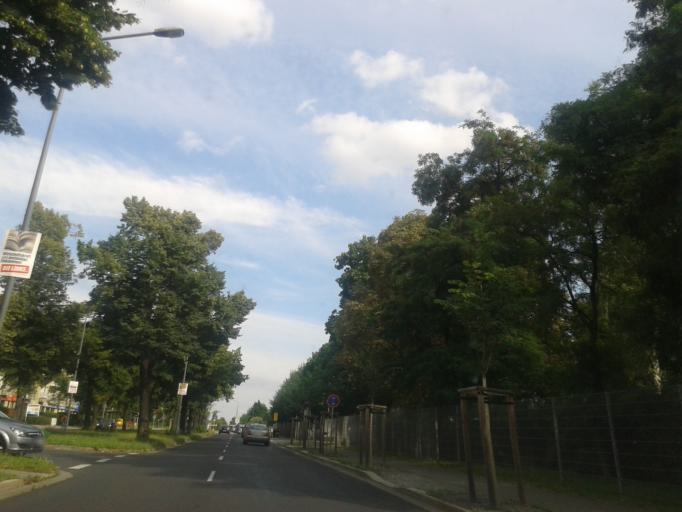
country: DE
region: Saxony
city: Dresden
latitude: 51.0304
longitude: 13.7815
